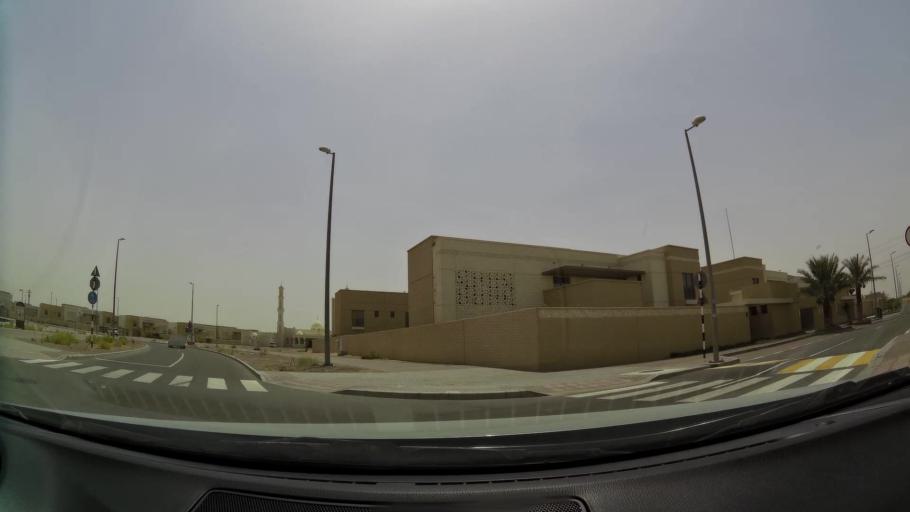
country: AE
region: Abu Dhabi
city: Al Ain
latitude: 24.1452
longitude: 55.6219
